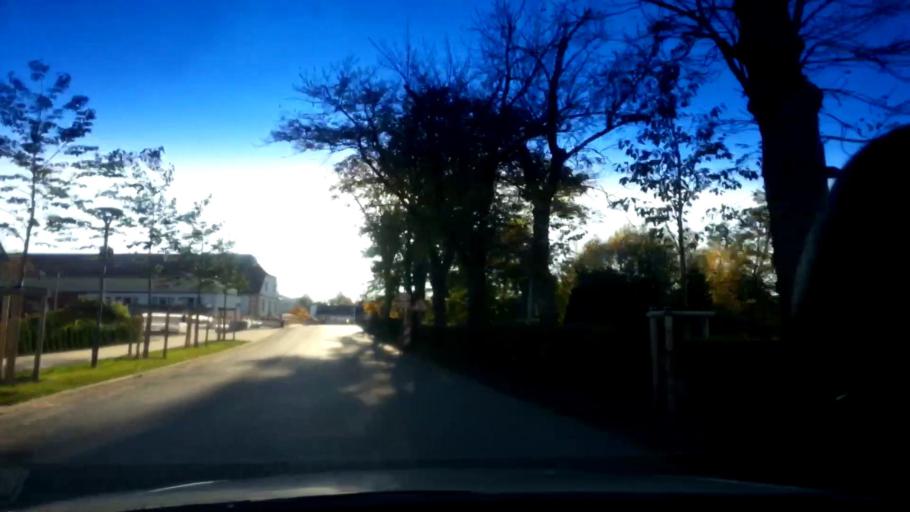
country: DE
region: Bavaria
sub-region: Upper Franconia
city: Baunach
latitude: 49.9888
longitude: 10.8531
